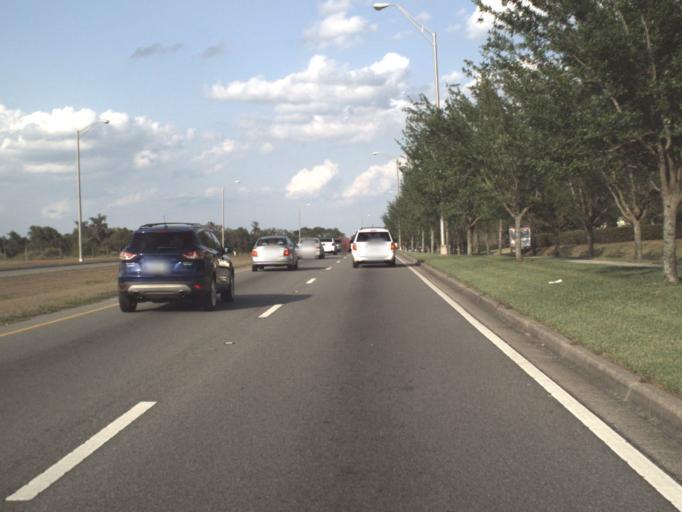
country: US
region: Florida
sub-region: Orange County
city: Maitland
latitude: 28.6334
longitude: -81.3735
